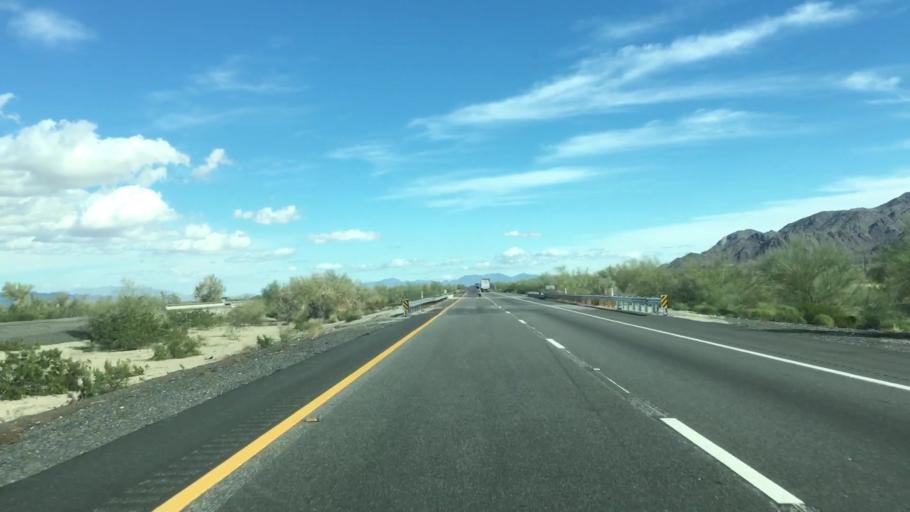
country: US
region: California
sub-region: Imperial County
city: Niland
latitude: 33.6826
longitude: -115.5405
